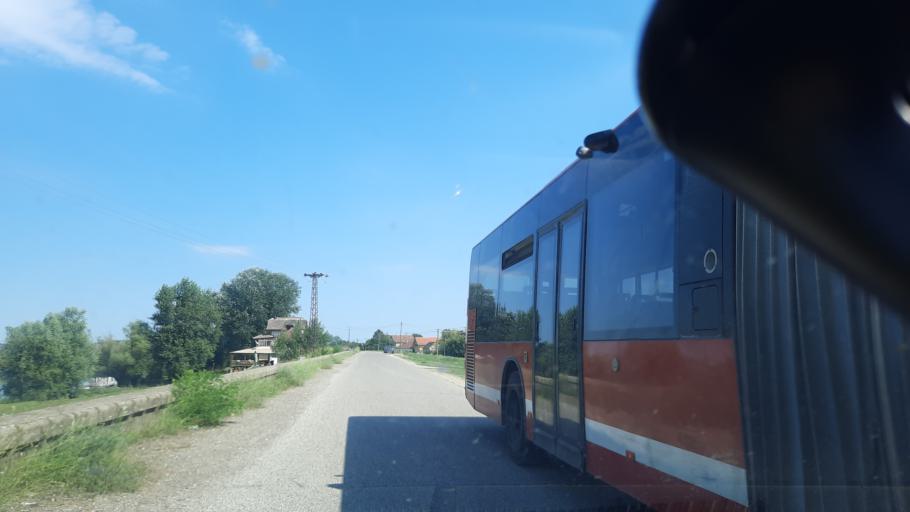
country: RS
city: Macvanska Mitrovica
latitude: 44.9595
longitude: 19.6056
